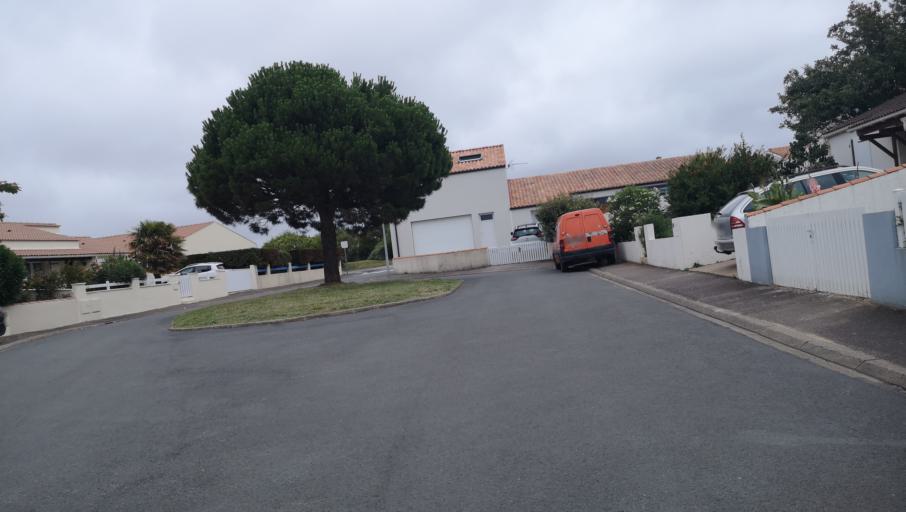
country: FR
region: Pays de la Loire
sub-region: Departement de la Vendee
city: Les Sables-d'Olonne
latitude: 46.5097
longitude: -1.7837
